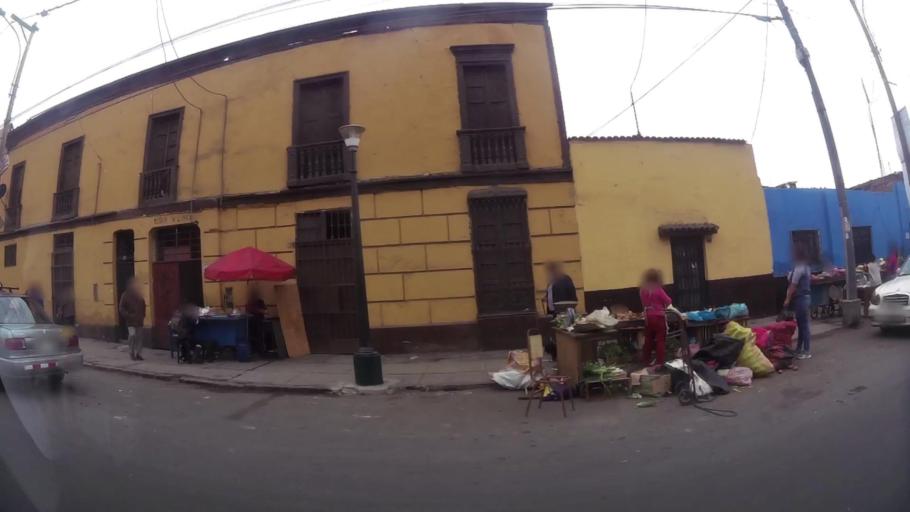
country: PE
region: Lima
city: Lima
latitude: -12.0458
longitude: -77.0148
